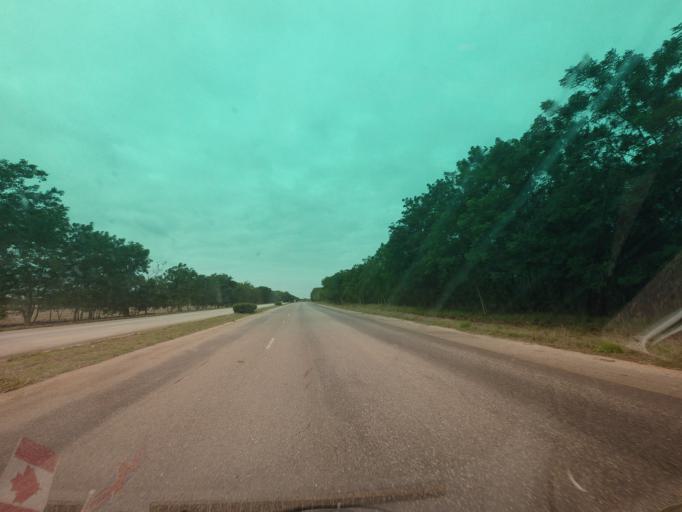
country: CU
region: Mayabeque
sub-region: Municipio de San Nicolas
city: San Nicolas de Bari
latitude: 22.7795
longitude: -81.8253
